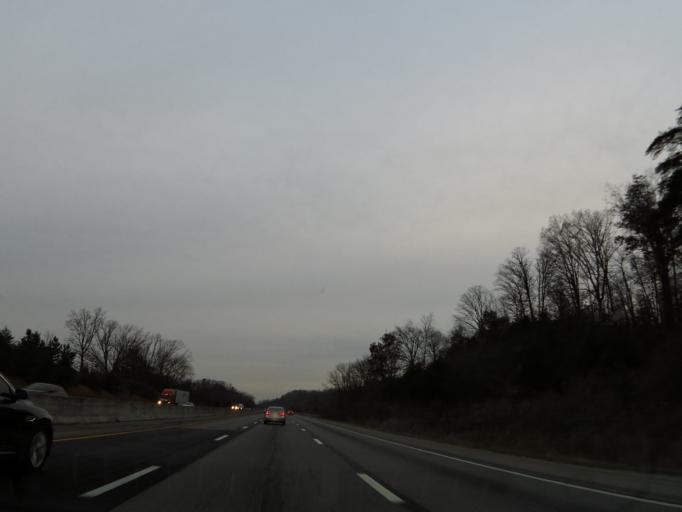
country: US
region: Kentucky
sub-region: Madison County
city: Berea
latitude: 37.5099
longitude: -84.3236
